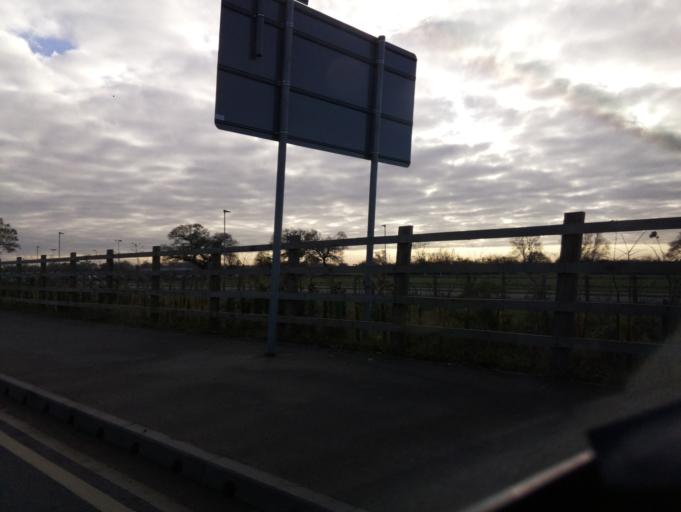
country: GB
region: England
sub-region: Staffordshire
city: Burton upon Trent
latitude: 52.7913
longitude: -1.6846
